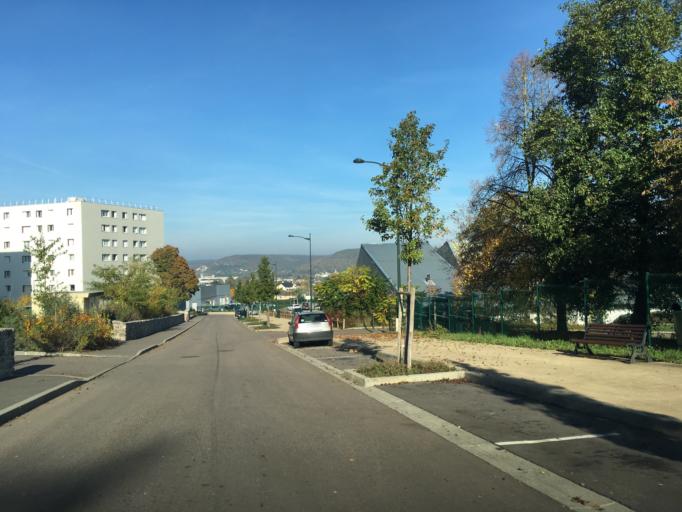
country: FR
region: Haute-Normandie
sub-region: Departement de l'Eure
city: Vernon
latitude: 49.0761
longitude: 1.4938
